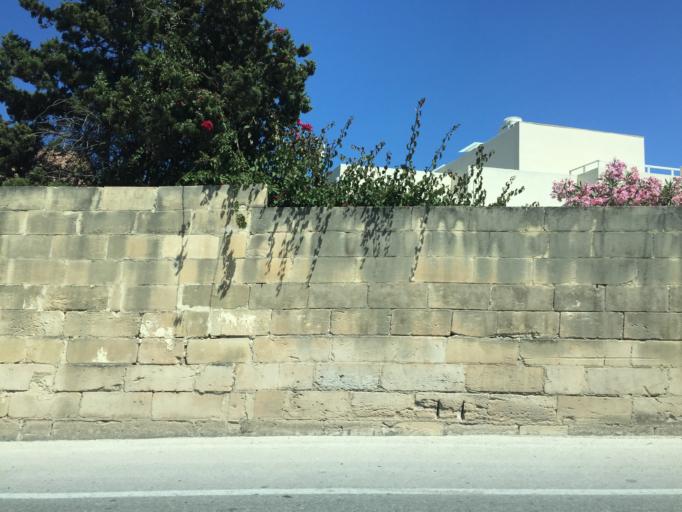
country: MT
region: Saint Julian
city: San Giljan
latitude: 35.9191
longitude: 14.4867
